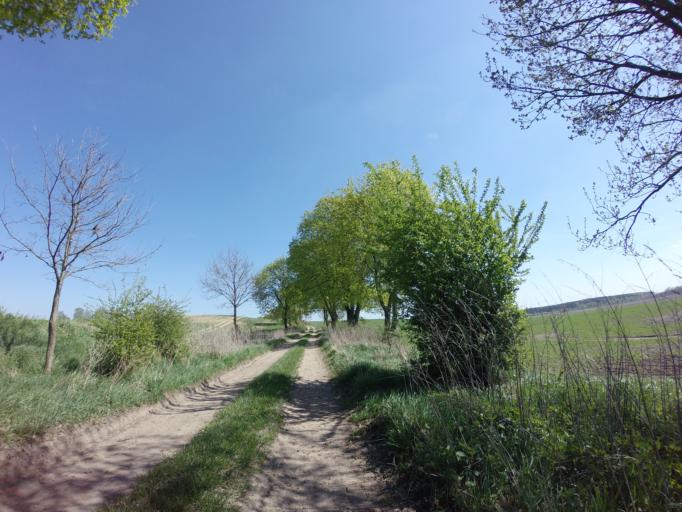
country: PL
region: West Pomeranian Voivodeship
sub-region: Powiat choszczenski
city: Choszczno
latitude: 53.1795
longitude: 15.3721
